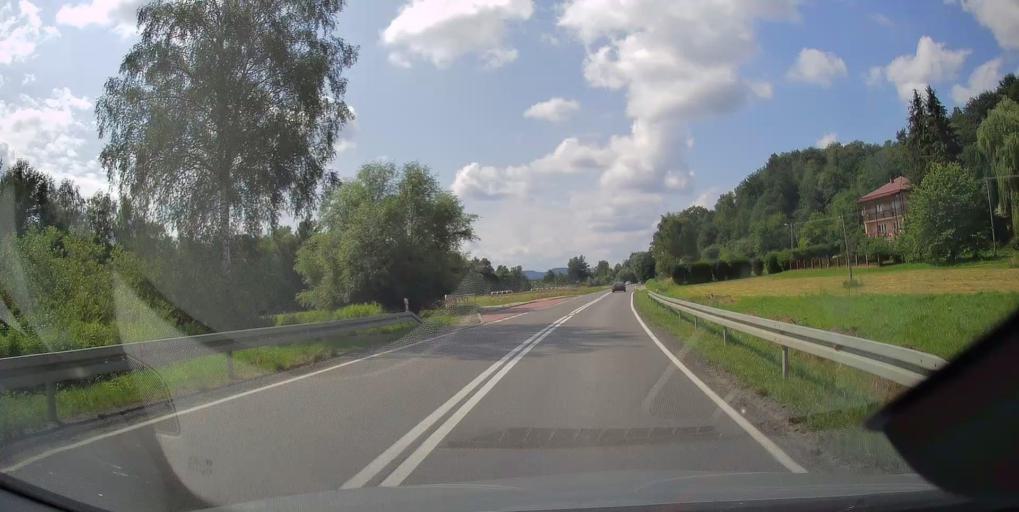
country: PL
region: Lesser Poland Voivodeship
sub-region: Powiat tarnowski
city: Janowice
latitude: 49.8819
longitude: 20.8322
